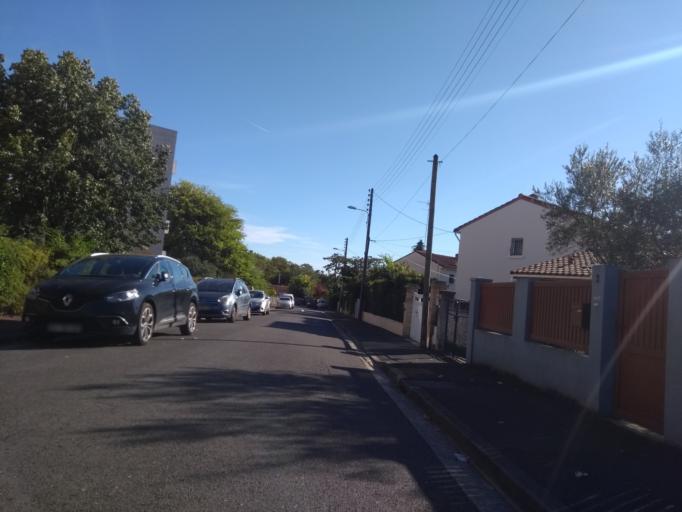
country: FR
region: Aquitaine
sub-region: Departement de la Gironde
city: Talence
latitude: 44.8118
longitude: -0.5799
